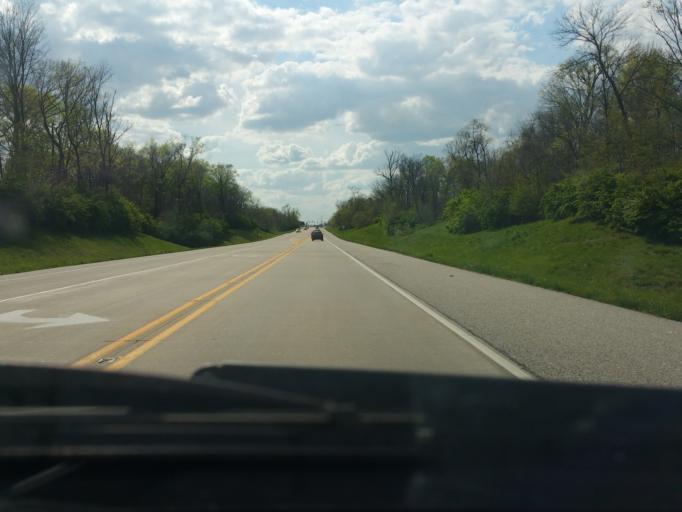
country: US
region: Illinois
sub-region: Madison County
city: Edwardsville
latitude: 38.7873
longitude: -89.9395
